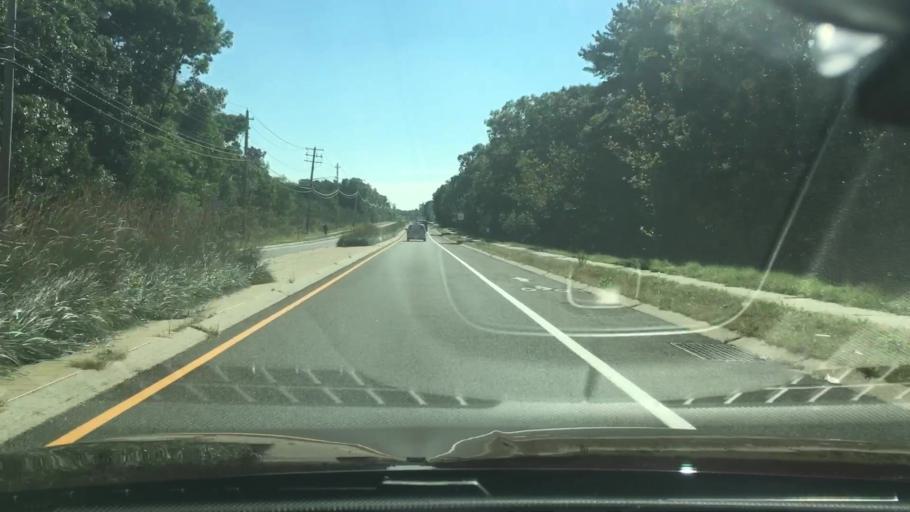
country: US
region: New York
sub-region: Suffolk County
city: Coram
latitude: 40.8975
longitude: -73.0201
